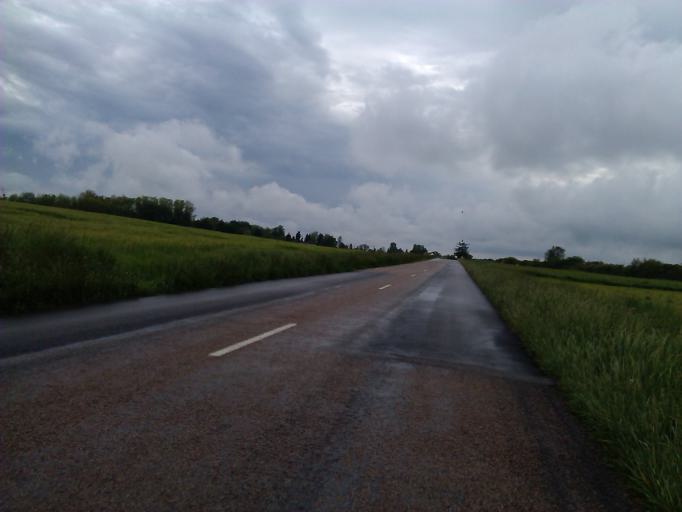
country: FR
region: Bourgogne
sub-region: Departement de Saone-et-Loire
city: Gergy
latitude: 46.8965
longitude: 4.9553
